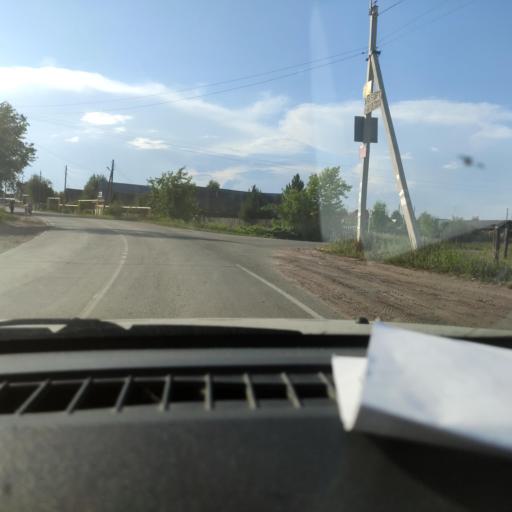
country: RU
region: Perm
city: Krasnokamsk
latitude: 58.1412
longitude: 55.7374
